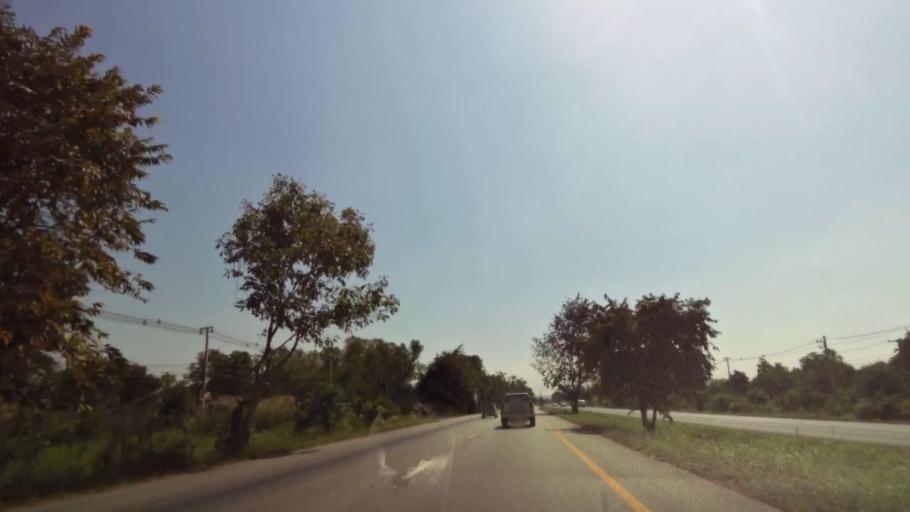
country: TH
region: Nakhon Sawan
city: Kao Liao
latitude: 15.8150
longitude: 100.1197
